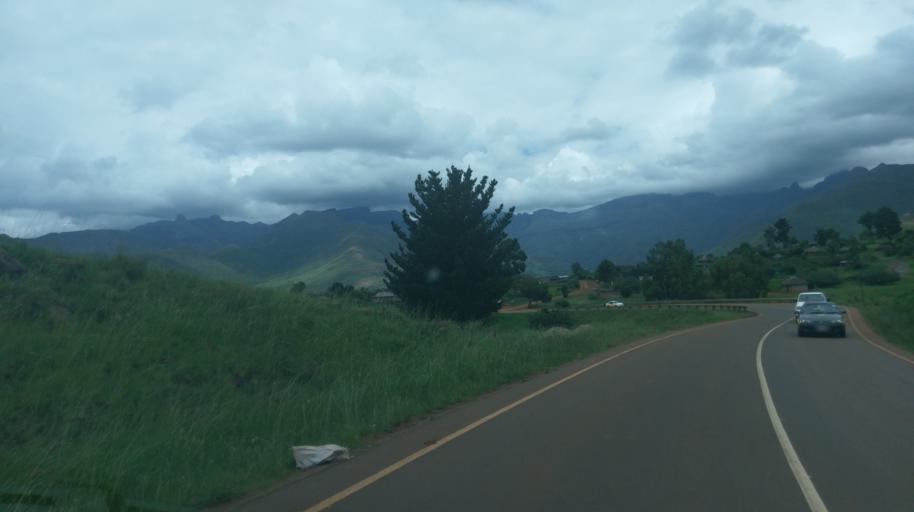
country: LS
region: Leribe
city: Leribe
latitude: -29.0391
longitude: 28.2414
